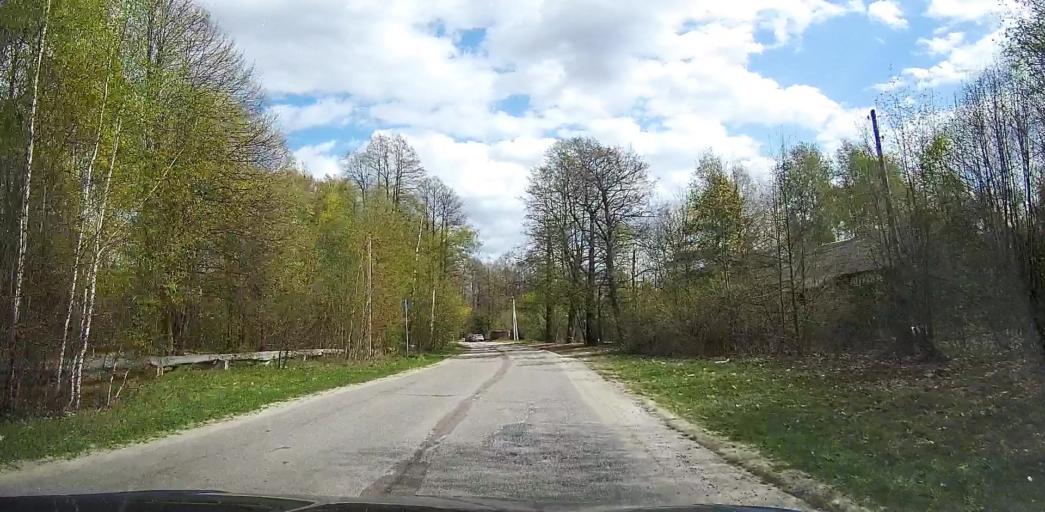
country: RU
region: Moskovskaya
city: Davydovo
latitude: 55.6479
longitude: 38.7573
